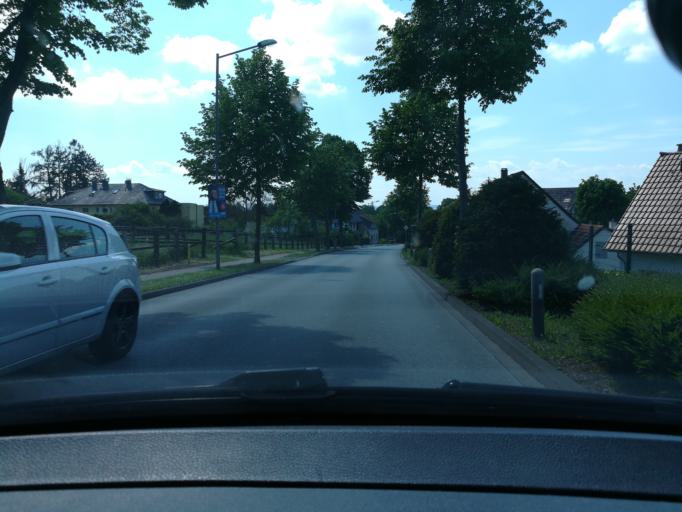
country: DE
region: North Rhine-Westphalia
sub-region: Regierungsbezirk Detmold
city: Herford
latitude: 52.1196
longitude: 8.7048
